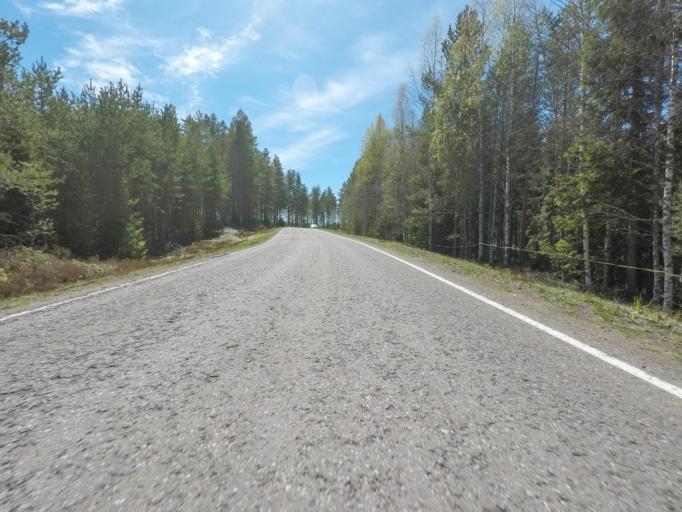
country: FI
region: Uusimaa
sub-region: Helsinki
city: Kaerkoelae
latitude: 60.6083
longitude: 23.8329
